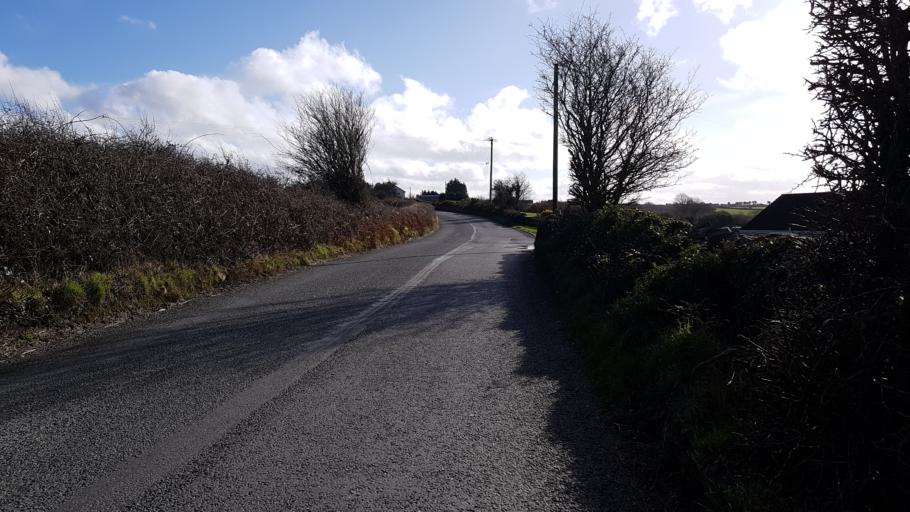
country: IE
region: Connaught
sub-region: County Galway
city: Gaillimh
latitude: 53.3113
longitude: -9.0220
